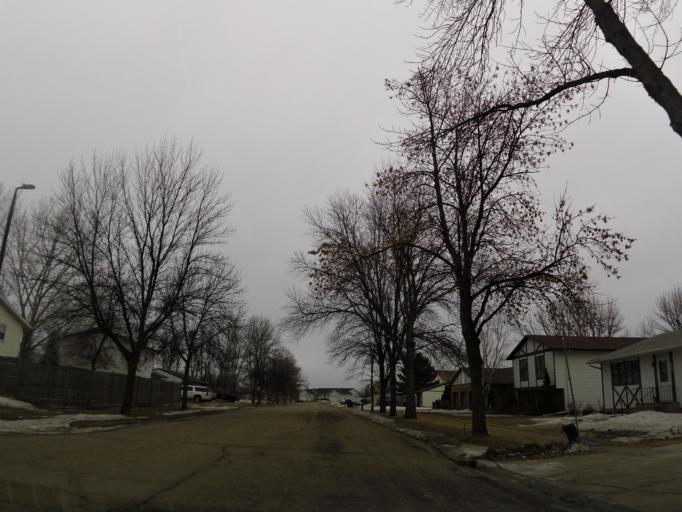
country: US
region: North Dakota
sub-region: Walsh County
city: Grafton
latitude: 48.4057
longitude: -97.4130
